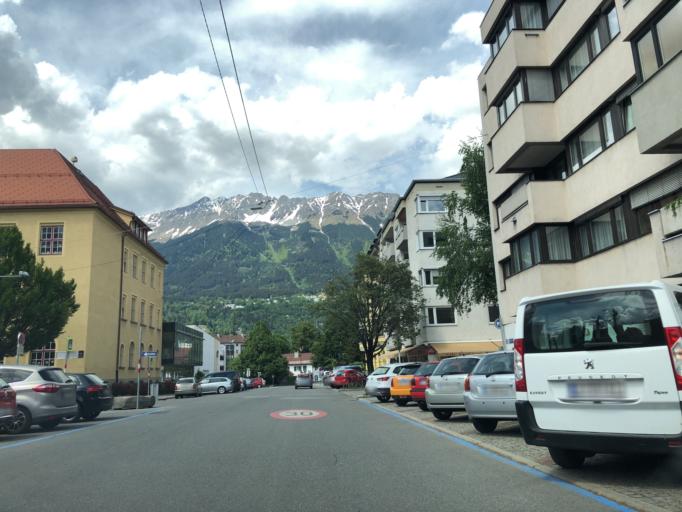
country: AT
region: Tyrol
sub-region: Innsbruck Stadt
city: Innsbruck
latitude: 47.2666
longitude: 11.4088
